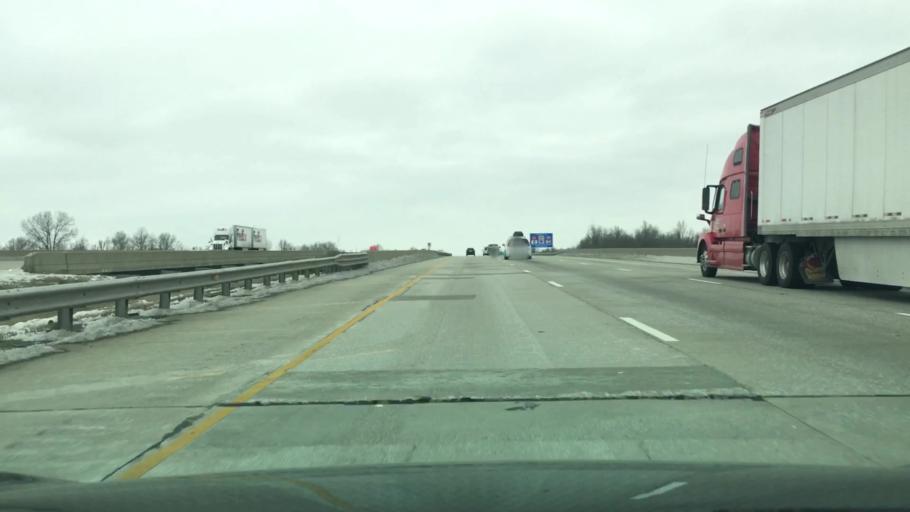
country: US
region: Illinois
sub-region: Jefferson County
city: Mount Vernon
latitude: 38.2833
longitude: -88.9391
